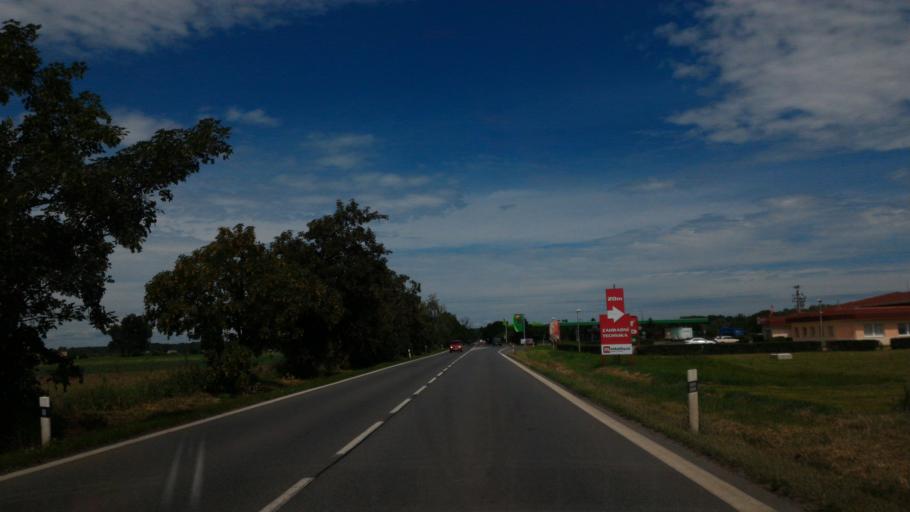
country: CZ
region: Central Bohemia
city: Libis
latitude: 50.2795
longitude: 14.4958
